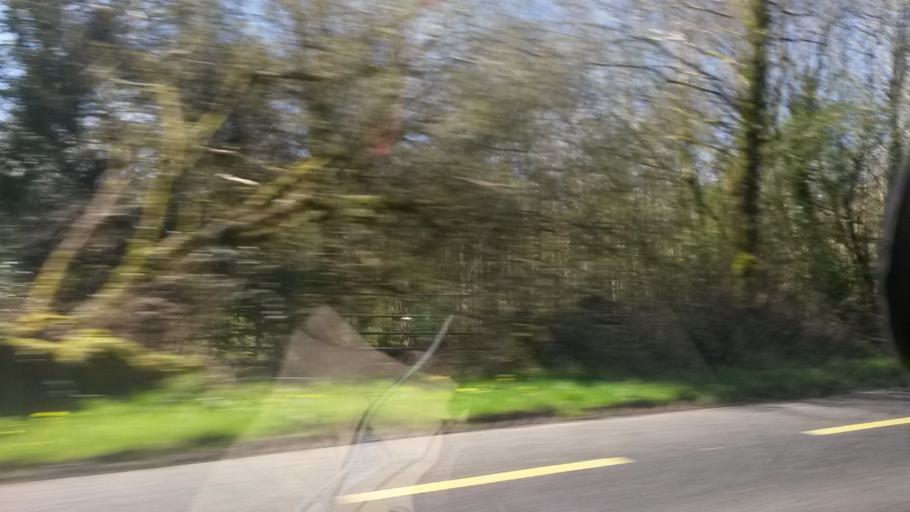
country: IE
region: Munster
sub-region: County Cork
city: Macroom
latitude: 51.9111
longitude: -9.0314
